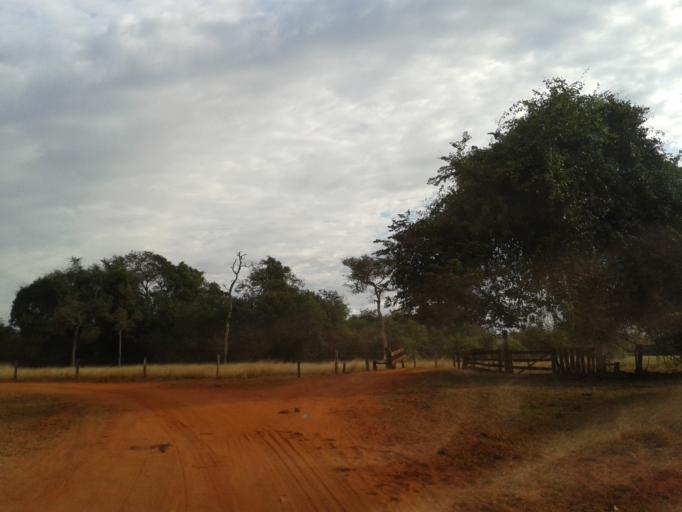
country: BR
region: Minas Gerais
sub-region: Santa Vitoria
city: Santa Vitoria
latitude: -18.7516
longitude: -50.1956
